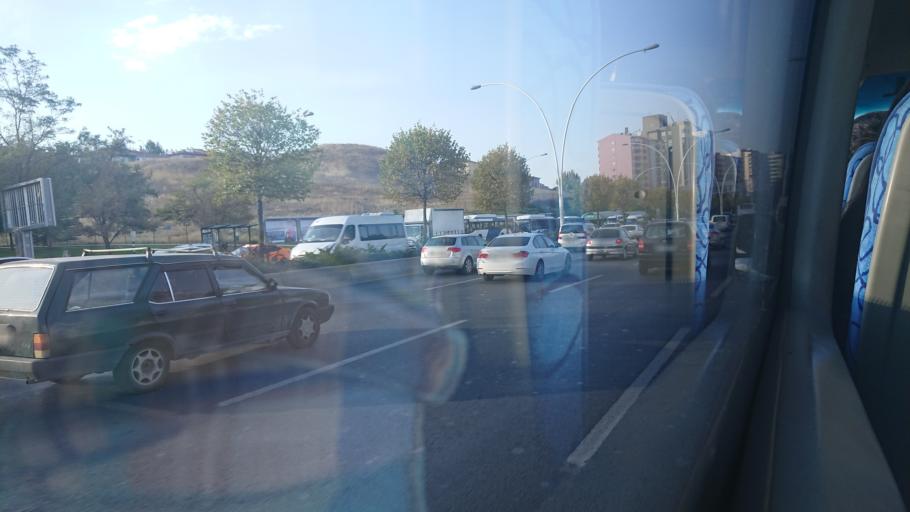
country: TR
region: Ankara
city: Ankara
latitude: 39.9221
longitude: 32.8143
